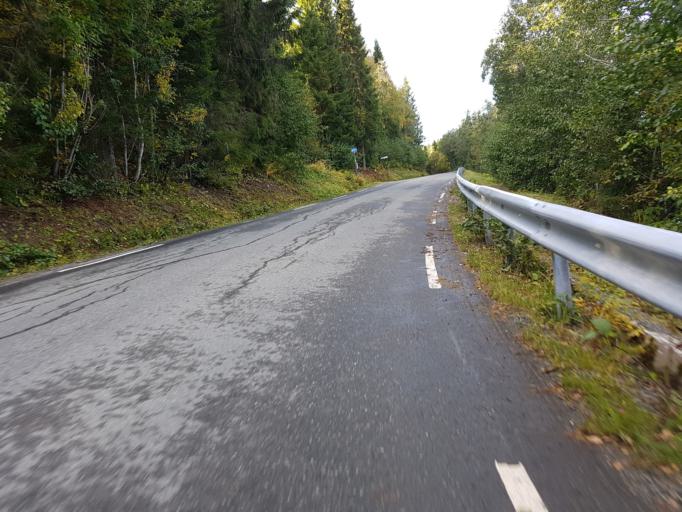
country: NO
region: Sor-Trondelag
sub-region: Klaebu
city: Klaebu
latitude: 63.3420
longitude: 10.5548
